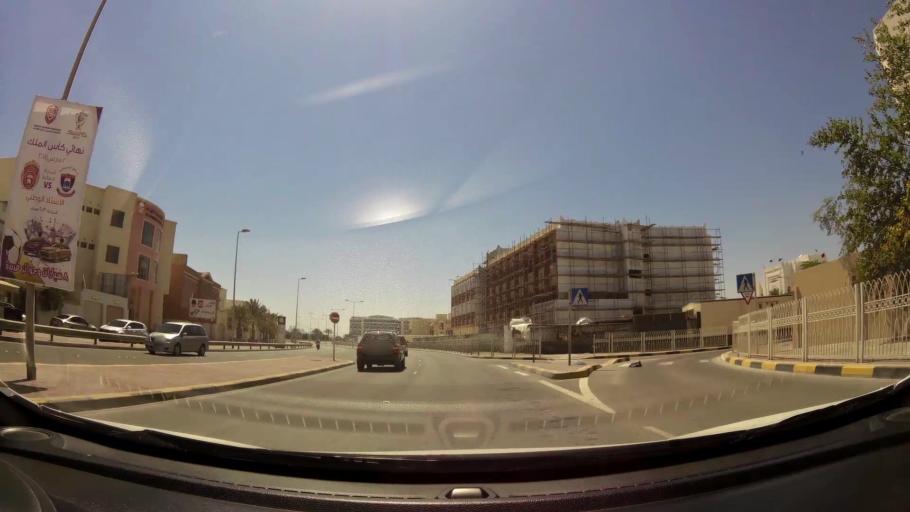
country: BH
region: Muharraq
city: Al Muharraq
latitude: 26.2690
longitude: 50.6030
